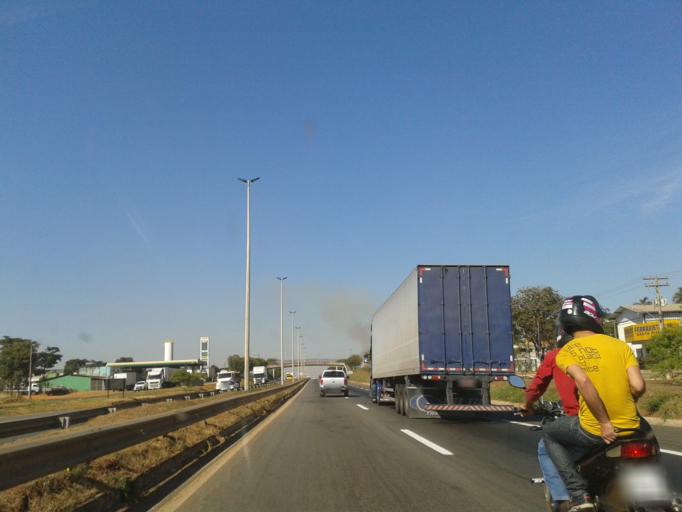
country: BR
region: Goias
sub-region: Aparecida De Goiania
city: Aparecida de Goiania
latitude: -16.8204
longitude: -49.2412
